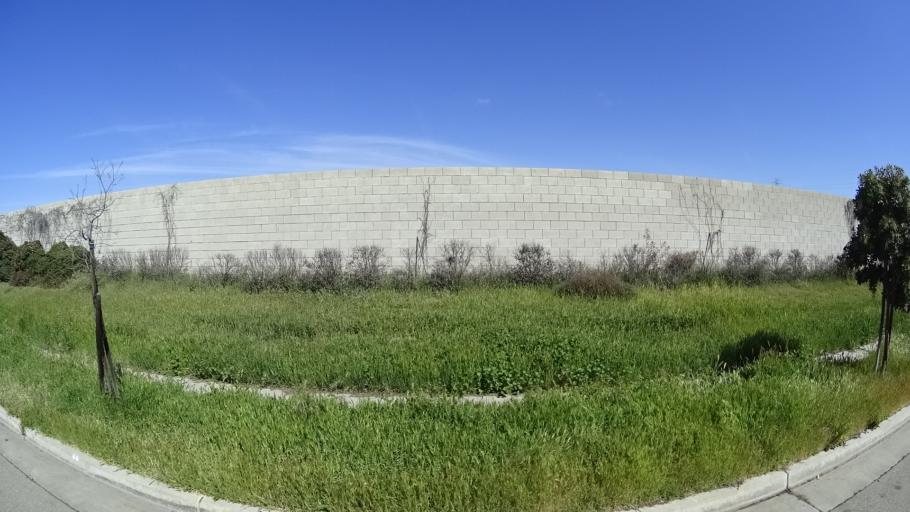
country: US
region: California
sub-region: Fresno County
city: Biola
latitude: 36.8181
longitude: -119.9026
